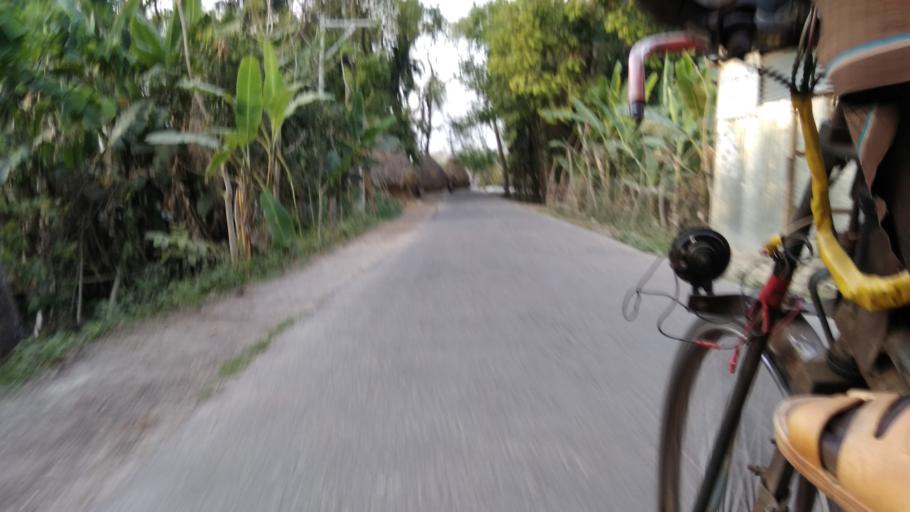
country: BD
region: Barisal
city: Mehendiganj
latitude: 22.9375
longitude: 90.4076
